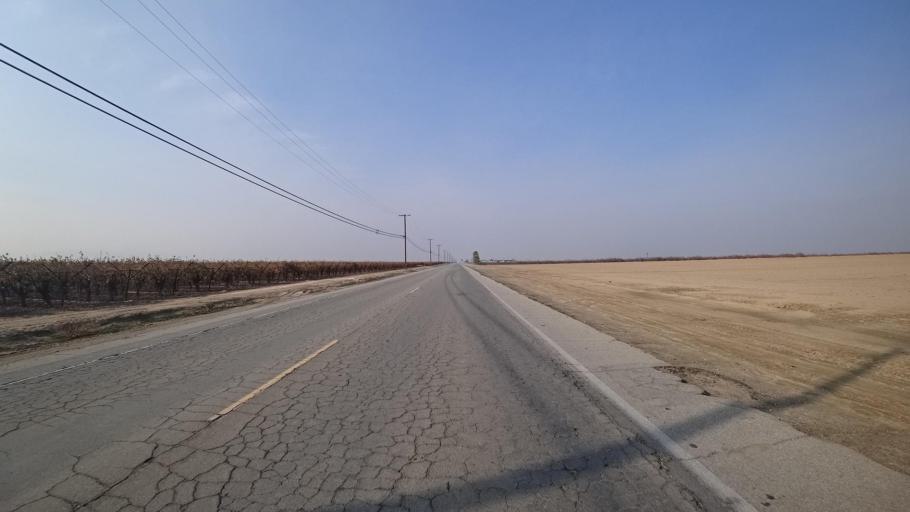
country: US
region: California
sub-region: Kern County
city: Weedpatch
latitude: 35.0930
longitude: -118.9208
